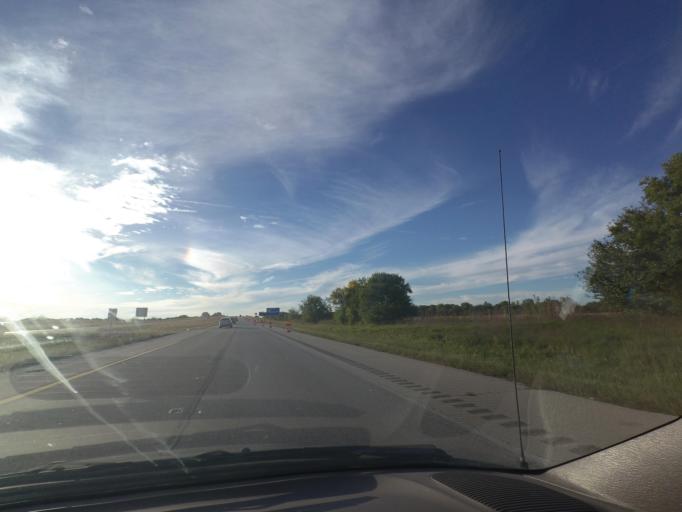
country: US
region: Illinois
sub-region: Sangamon County
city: Jerome
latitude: 39.7486
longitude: -89.7243
